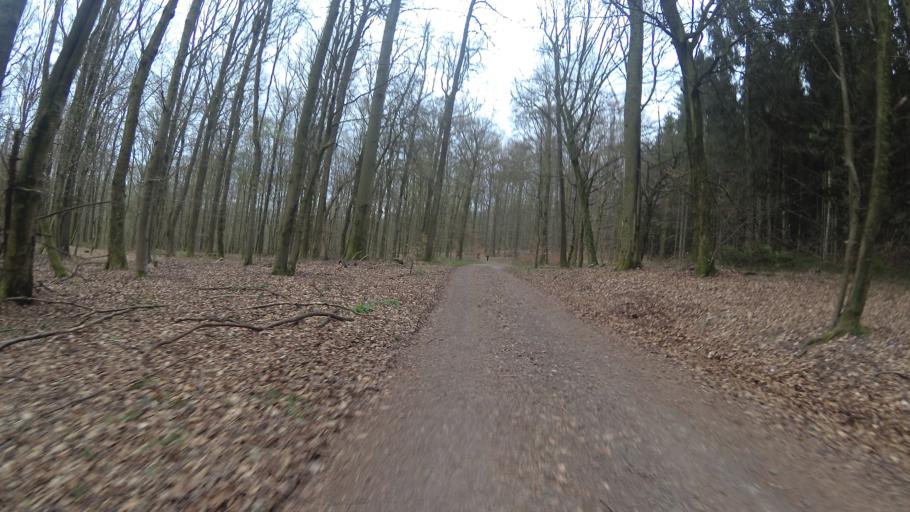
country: DE
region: Saarland
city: Hangard
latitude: 49.4332
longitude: 7.2117
